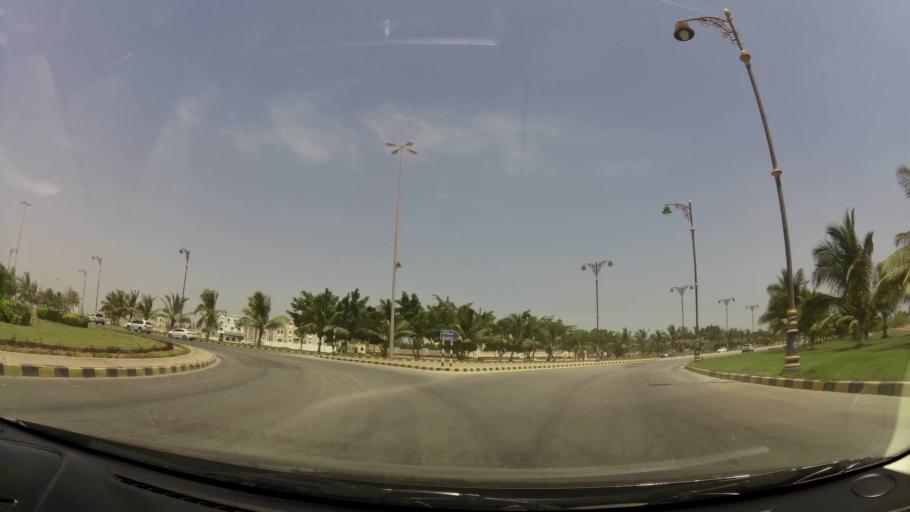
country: OM
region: Zufar
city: Salalah
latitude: 17.0685
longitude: 54.1461
